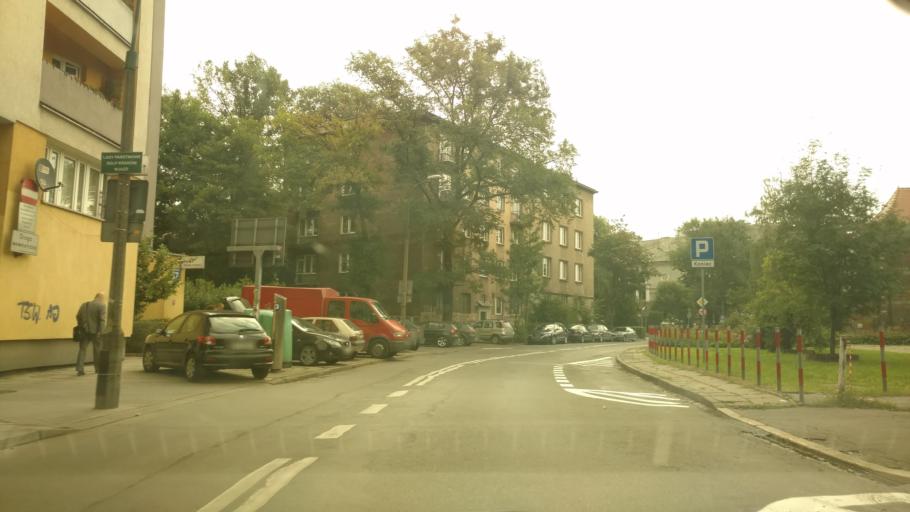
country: PL
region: Lesser Poland Voivodeship
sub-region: Krakow
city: Krakow
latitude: 50.0712
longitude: 19.9305
